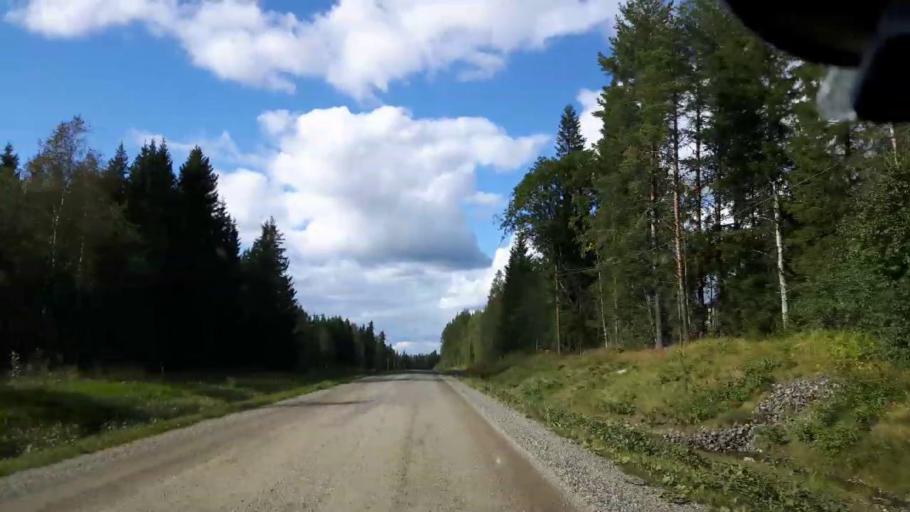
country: SE
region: Jaemtland
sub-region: Stroemsunds Kommun
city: Stroemsund
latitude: 63.3332
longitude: 15.5763
